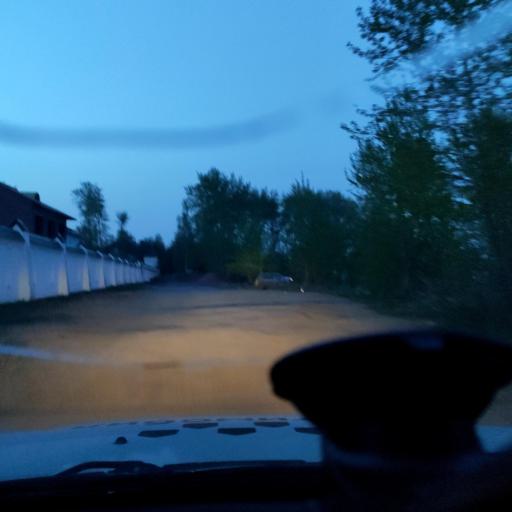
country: RU
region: Perm
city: Perm
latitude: 58.0473
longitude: 56.2926
